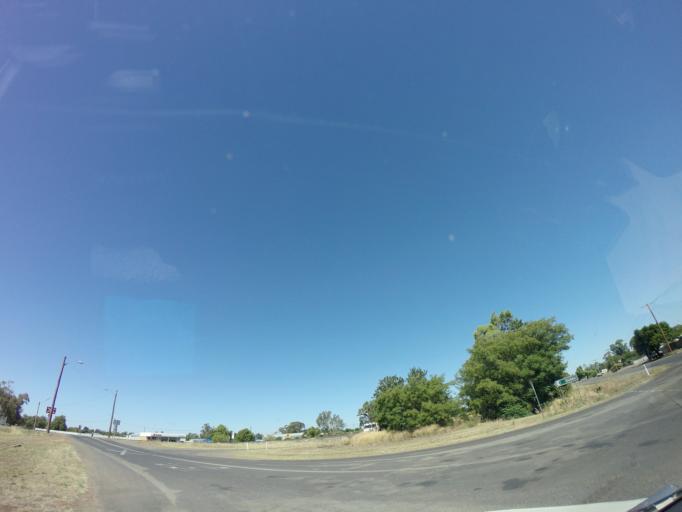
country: AU
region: New South Wales
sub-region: Bogan
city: Nyngan
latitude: -31.5656
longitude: 147.2012
